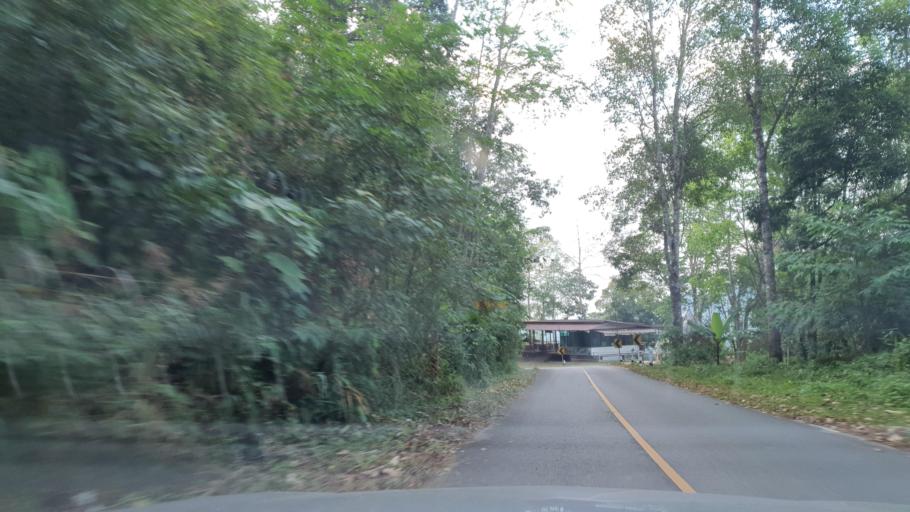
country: TH
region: Chiang Mai
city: Mae On
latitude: 18.9405
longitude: 99.3675
